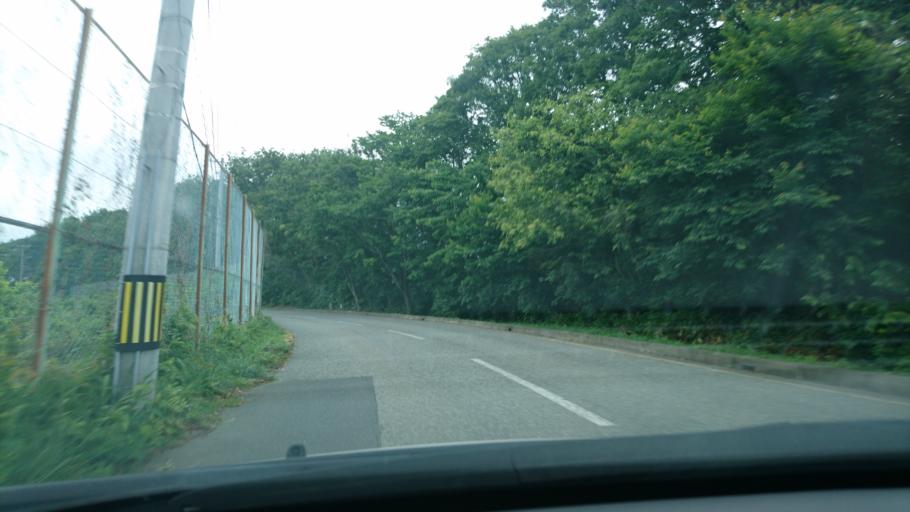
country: JP
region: Iwate
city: Ichinoseki
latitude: 38.9062
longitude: 141.1546
